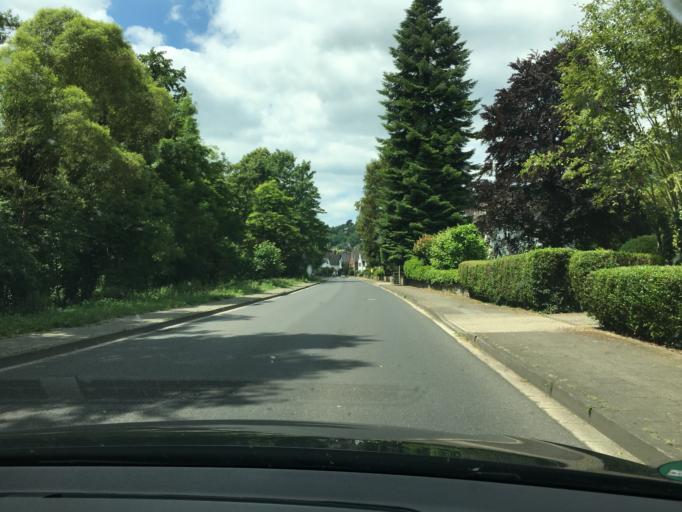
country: DE
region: North Rhine-Westphalia
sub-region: Regierungsbezirk Koln
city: Kreuzau
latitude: 50.7279
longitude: 6.4664
